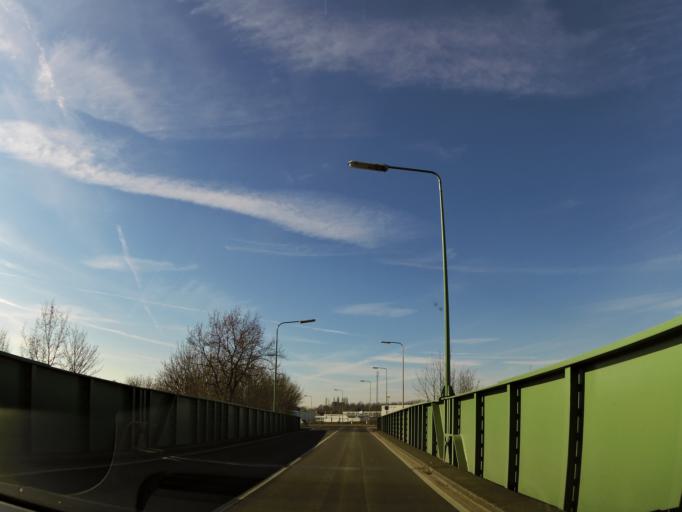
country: NL
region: Limburg
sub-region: Gemeente Sittard-Geleen
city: Born
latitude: 51.0375
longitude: 5.8083
